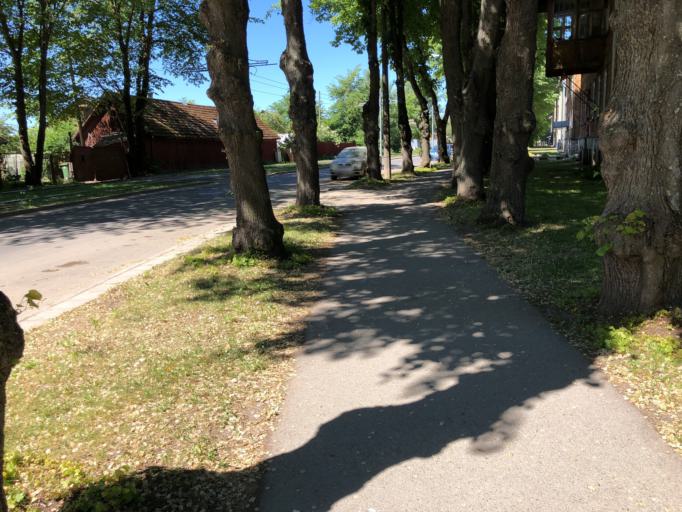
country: EE
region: Harju
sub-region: Tallinna linn
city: Tallinn
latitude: 59.4430
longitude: 24.7251
